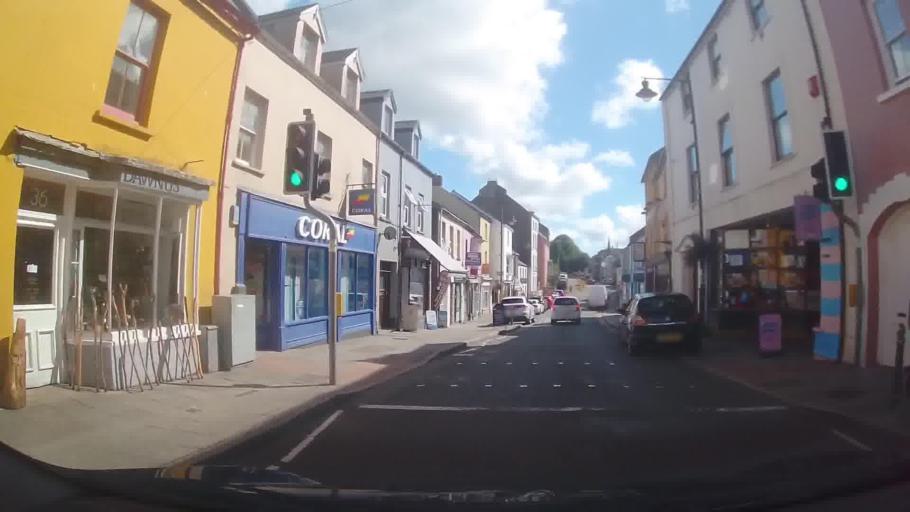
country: GB
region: Wales
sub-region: Pembrokeshire
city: Pembroke
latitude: 51.6756
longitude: -4.9162
